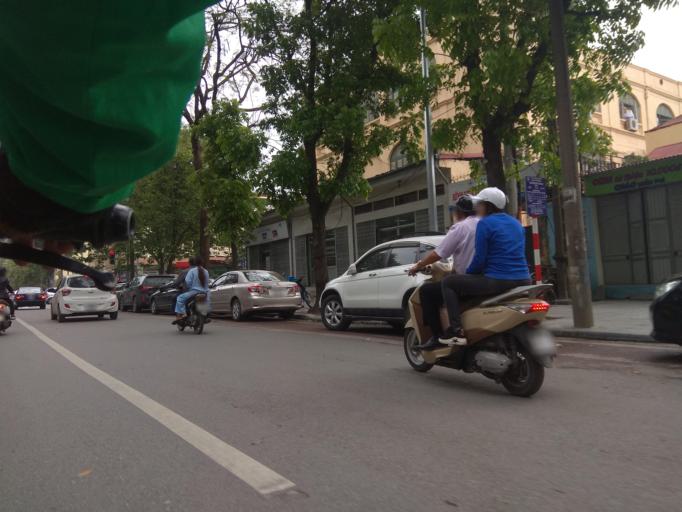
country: VN
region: Ha Noi
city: Hoan Kiem
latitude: 21.0246
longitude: 105.8496
